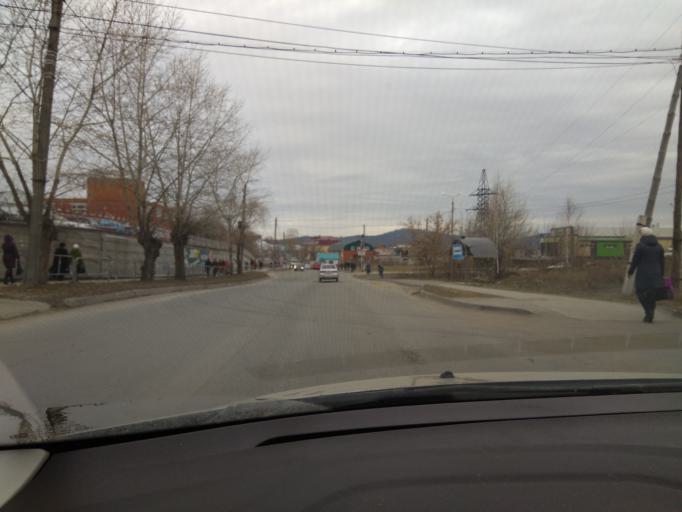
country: RU
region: Chelyabinsk
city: Kyshtym
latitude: 55.7071
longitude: 60.5686
